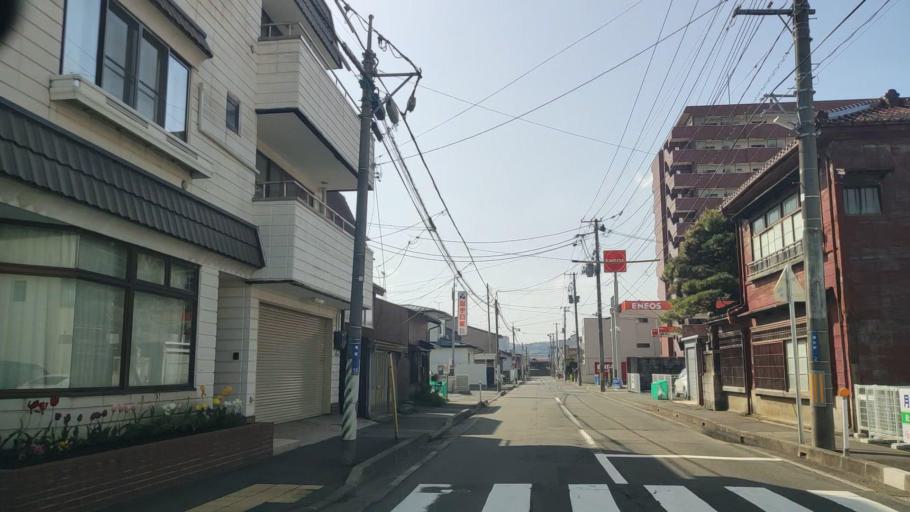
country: JP
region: Iwate
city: Morioka-shi
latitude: 39.6966
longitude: 141.1532
